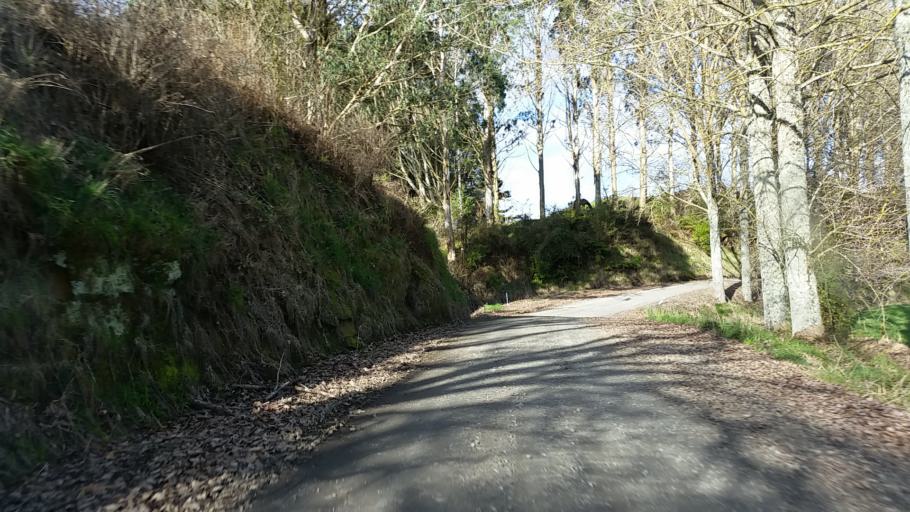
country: NZ
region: Taranaki
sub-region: South Taranaki District
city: Eltham
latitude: -39.2533
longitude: 174.5110
